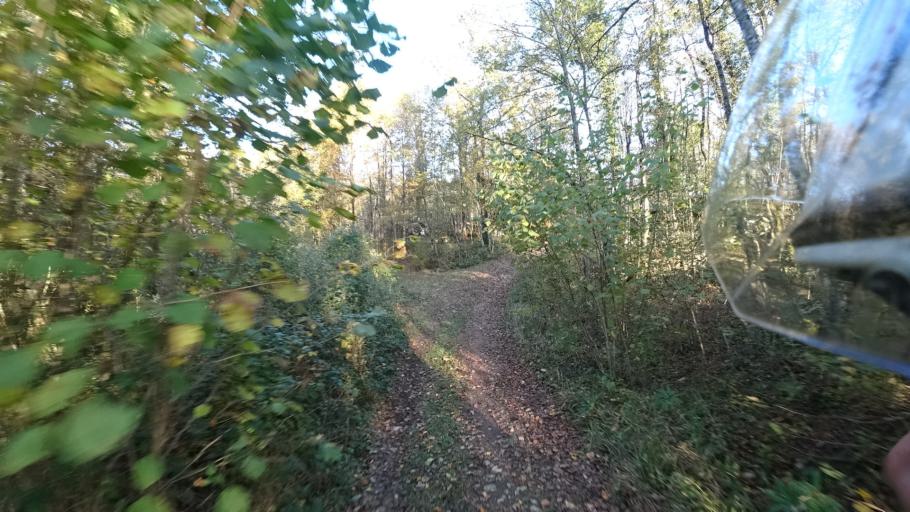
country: HR
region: Primorsko-Goranska
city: Matulji
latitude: 45.4022
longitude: 14.3103
